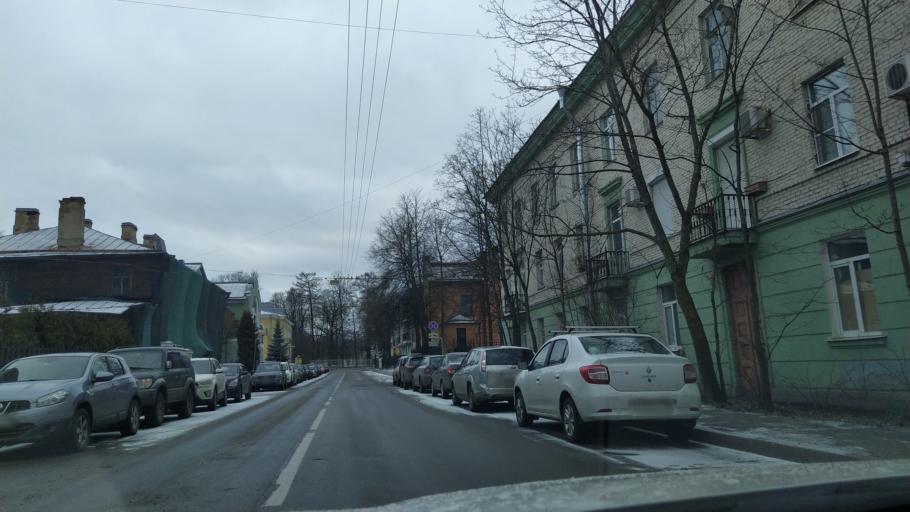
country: RU
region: St.-Petersburg
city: Pushkin
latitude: 59.7204
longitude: 30.3984
